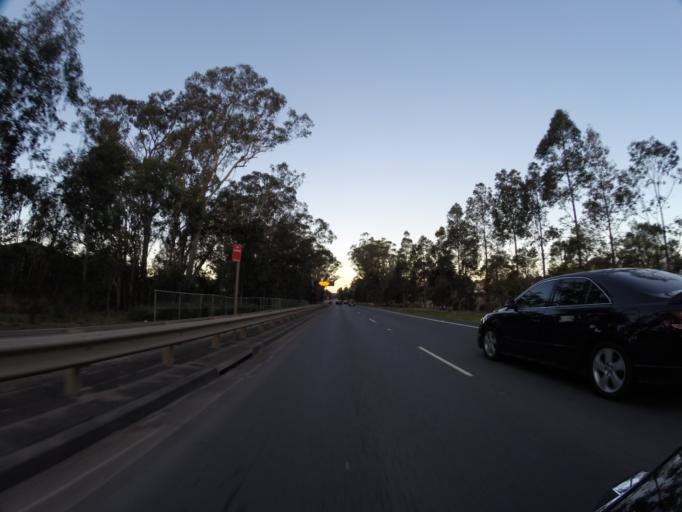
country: AU
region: New South Wales
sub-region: Campbelltown Municipality
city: Glenfield
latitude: -33.9557
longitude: 150.8688
